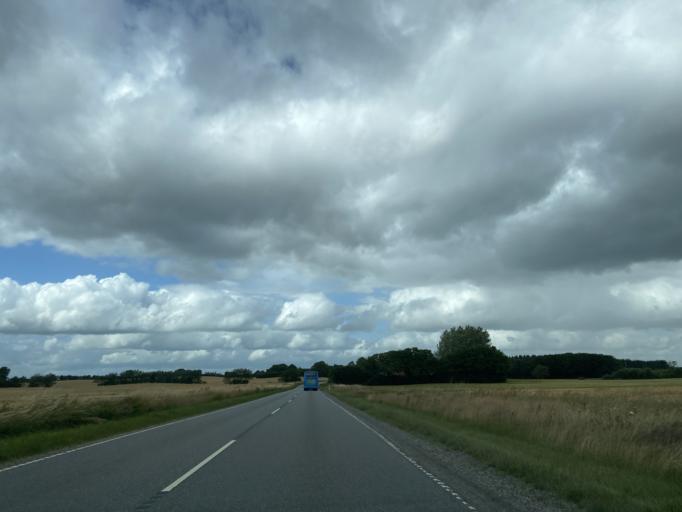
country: DK
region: Central Jutland
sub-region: Silkeborg Kommune
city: Silkeborg
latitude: 56.2436
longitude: 9.6242
